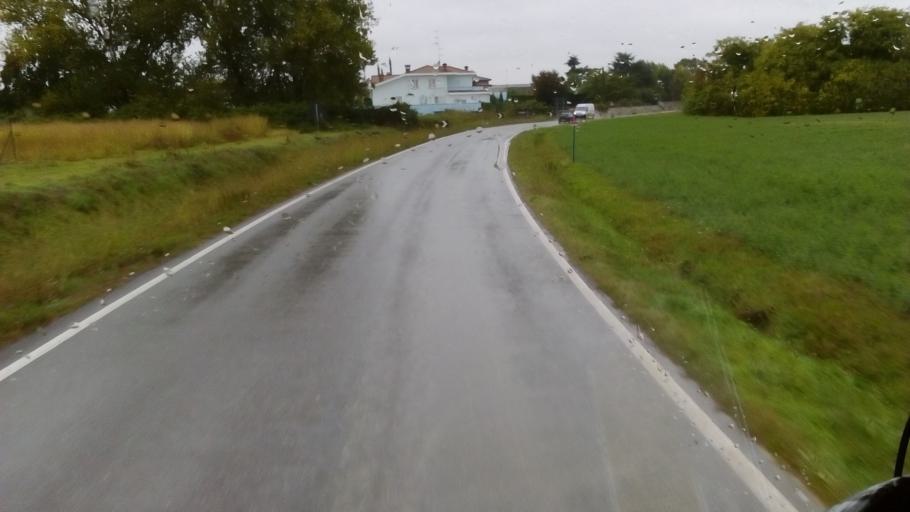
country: IT
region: Emilia-Romagna
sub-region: Provincia di Reggio Emilia
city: Luzzara
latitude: 44.9479
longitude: 10.7086
